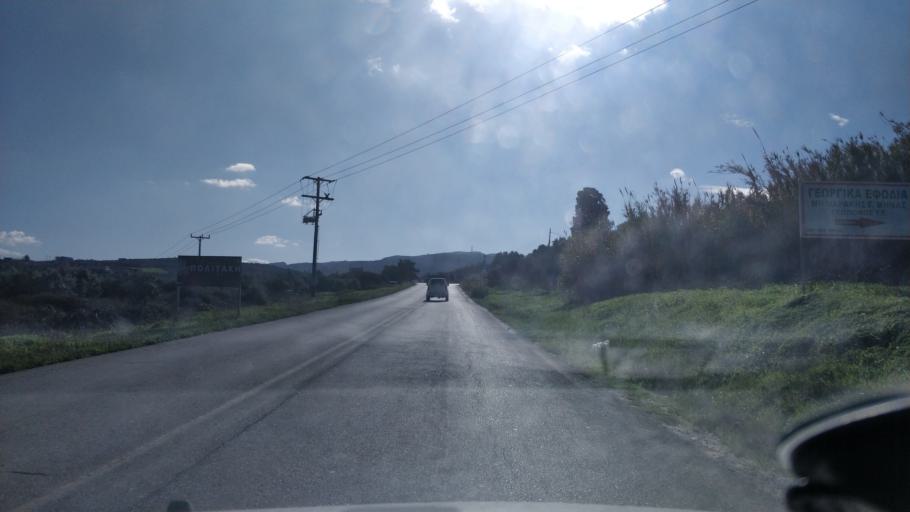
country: GR
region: Crete
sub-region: Nomos Irakleiou
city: Ano Arhanes
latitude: 35.2149
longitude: 25.1974
